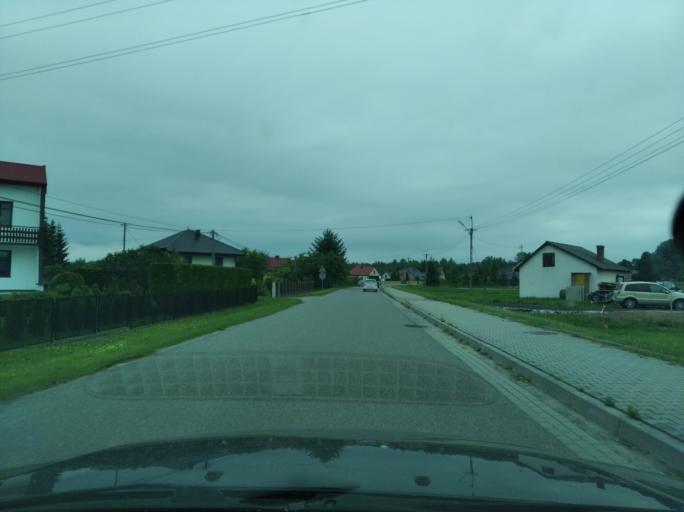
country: PL
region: Subcarpathian Voivodeship
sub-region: Powiat kolbuszowski
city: Niwiska
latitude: 50.1556
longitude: 21.6697
